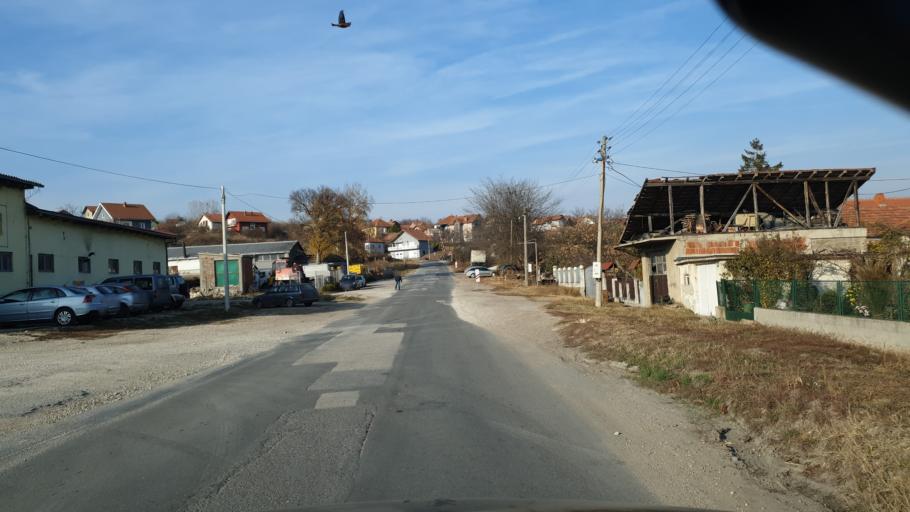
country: RS
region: Central Serbia
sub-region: Zajecarski Okrug
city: Zajecar
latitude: 43.9176
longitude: 22.2907
